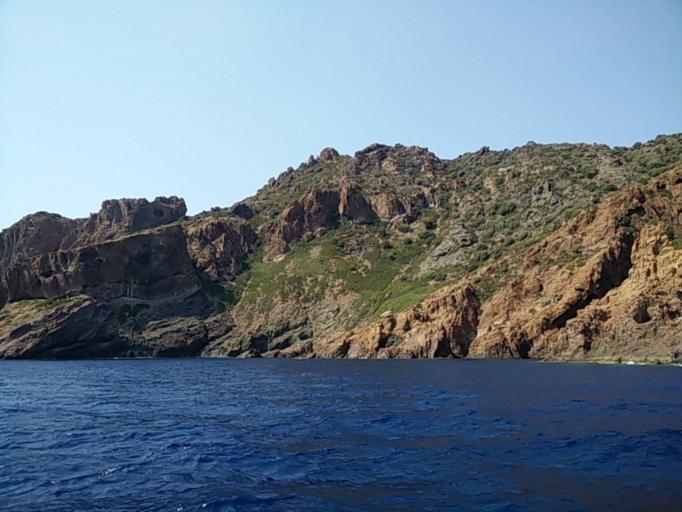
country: FR
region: Corsica
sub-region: Departement de la Corse-du-Sud
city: Cargese
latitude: 42.3320
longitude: 8.5622
